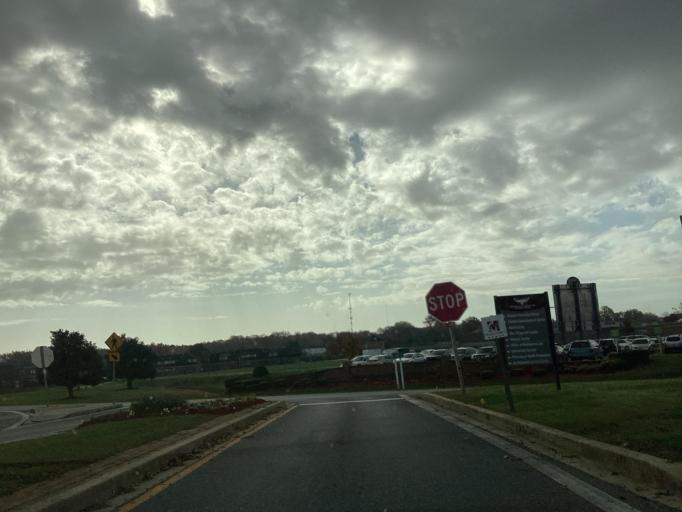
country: US
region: Maryland
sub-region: Somerset County
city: Princess Anne
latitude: 38.2133
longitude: -75.6862
